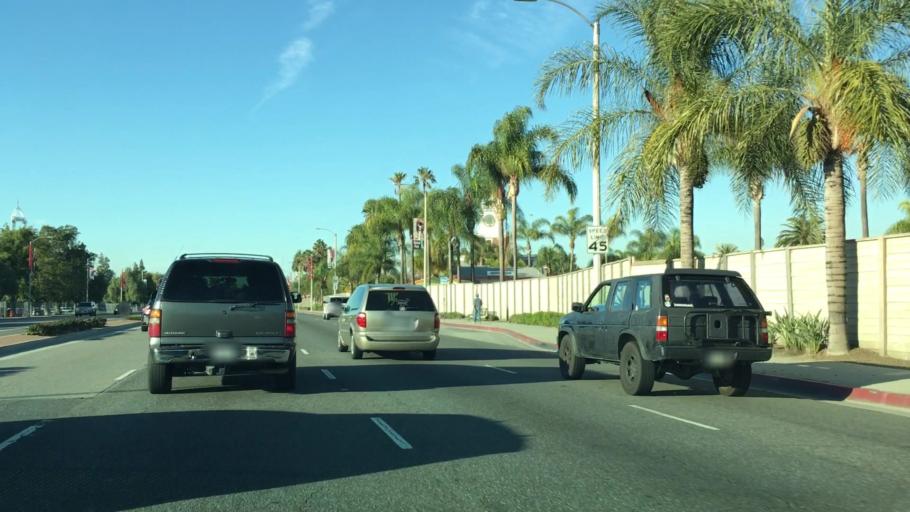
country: US
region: California
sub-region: Orange County
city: Buena Park
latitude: 33.8397
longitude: -117.9955
